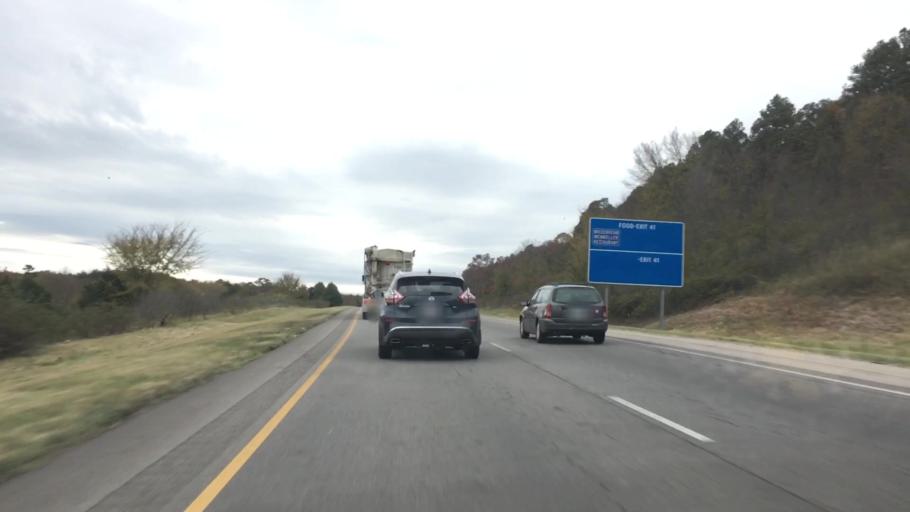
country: US
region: Arkansas
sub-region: Johnson County
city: Coal Hill
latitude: 35.5033
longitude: -93.7323
